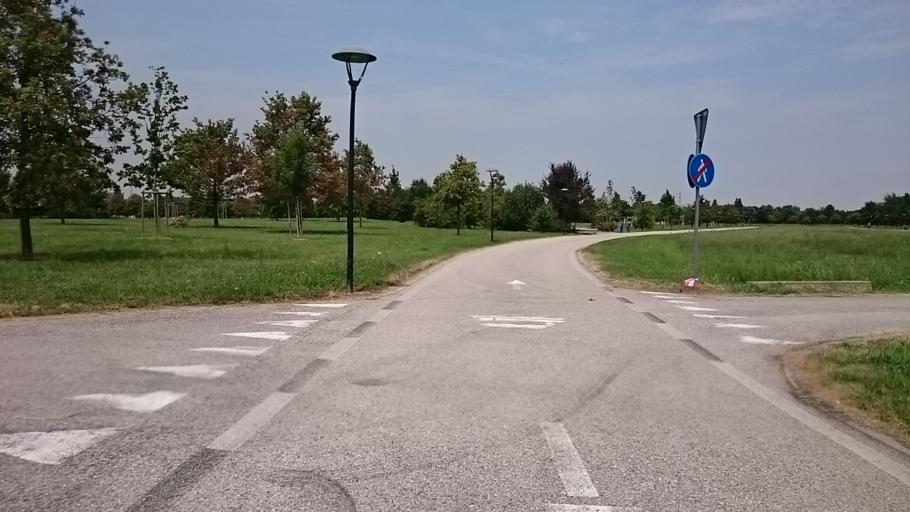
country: IT
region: Veneto
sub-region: Provincia di Venezia
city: Campalto
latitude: 45.4719
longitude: 12.2740
